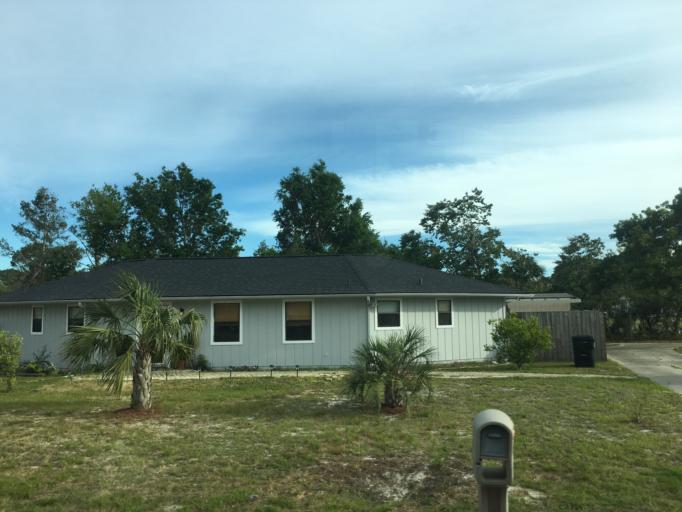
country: US
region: Florida
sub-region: Bay County
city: Upper Grand Lagoon
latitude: 30.1683
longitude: -85.7672
